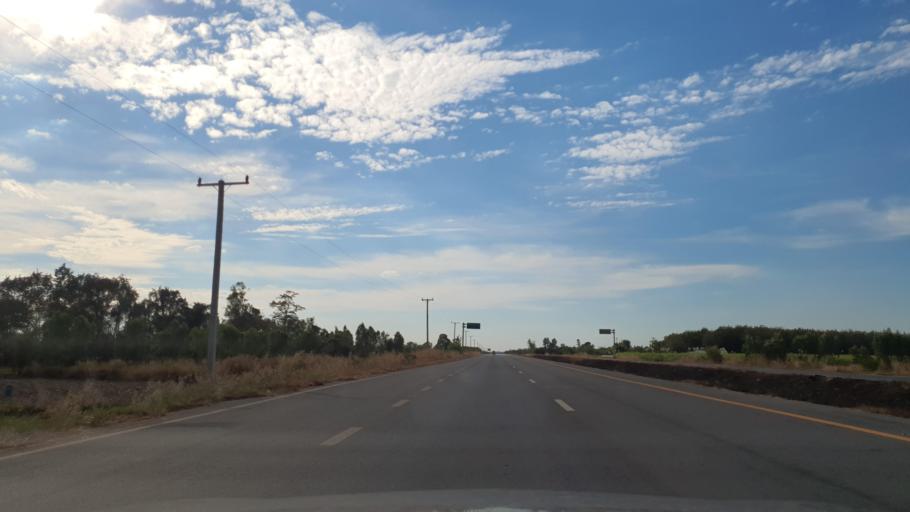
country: TH
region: Roi Et
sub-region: Amphoe Pho Chai
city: Pho Chai
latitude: 16.4147
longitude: 103.8022
